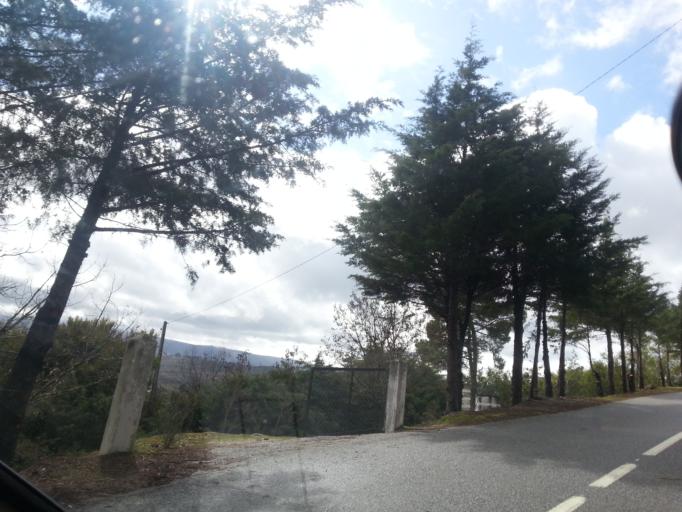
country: PT
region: Guarda
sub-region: Fornos de Algodres
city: Fornos de Algodres
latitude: 40.6170
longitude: -7.4825
